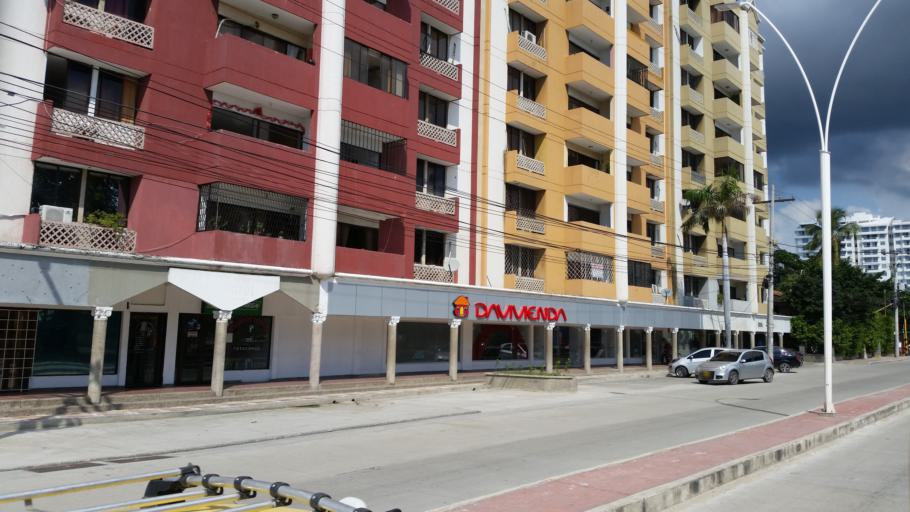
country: CO
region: Magdalena
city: Santa Marta
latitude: 11.2413
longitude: -74.1949
